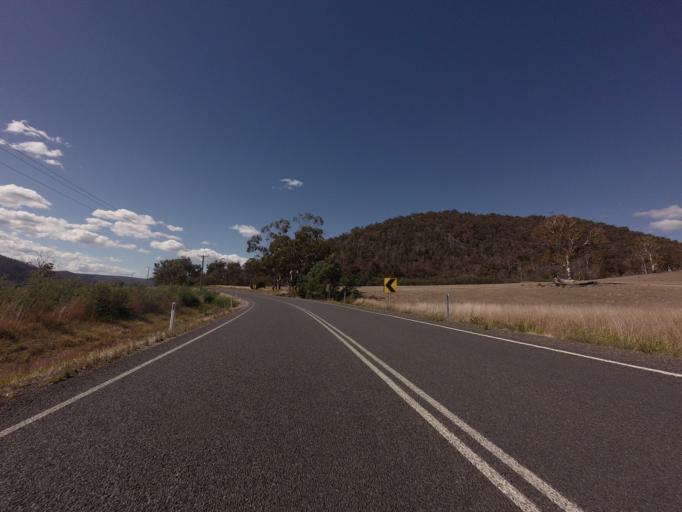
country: AU
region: Tasmania
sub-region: Break O'Day
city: St Helens
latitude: -41.6894
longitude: 147.8790
